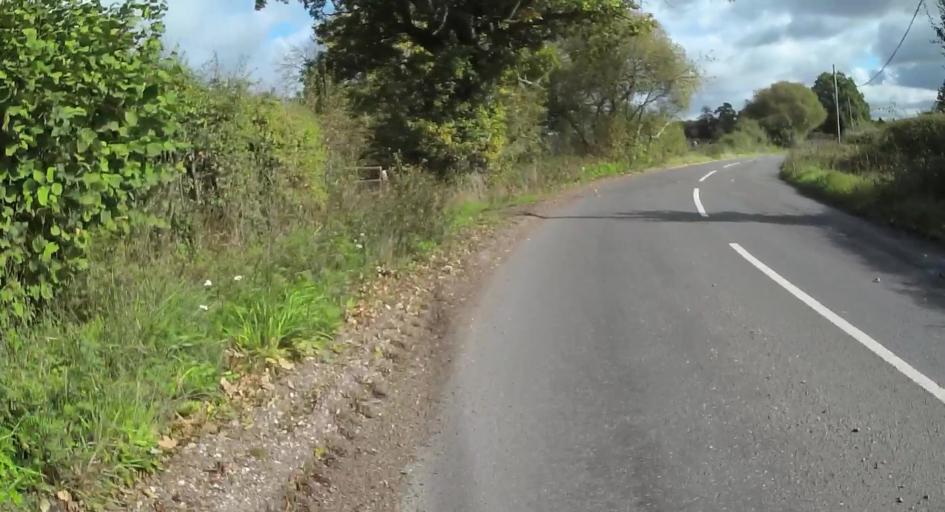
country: GB
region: England
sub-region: Hampshire
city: Odiham
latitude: 51.2813
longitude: -0.8919
